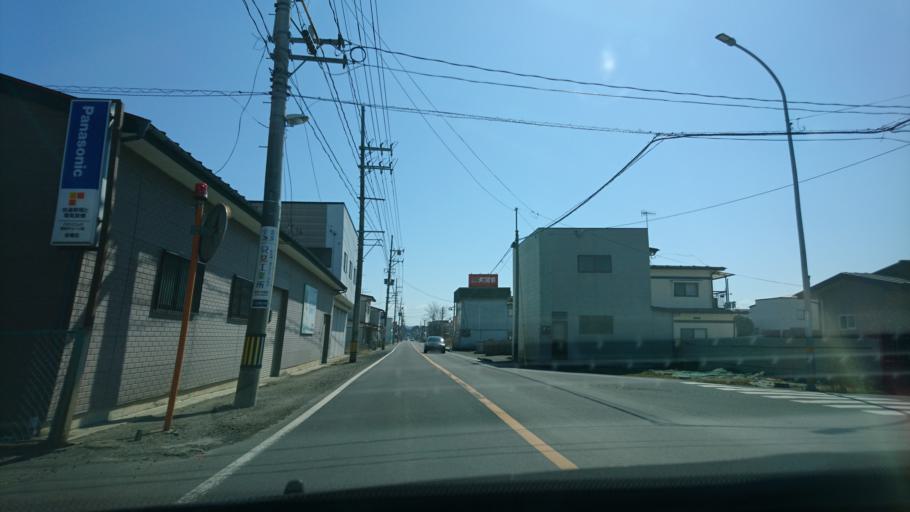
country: JP
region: Iwate
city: Ichinoseki
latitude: 38.7710
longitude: 141.1471
